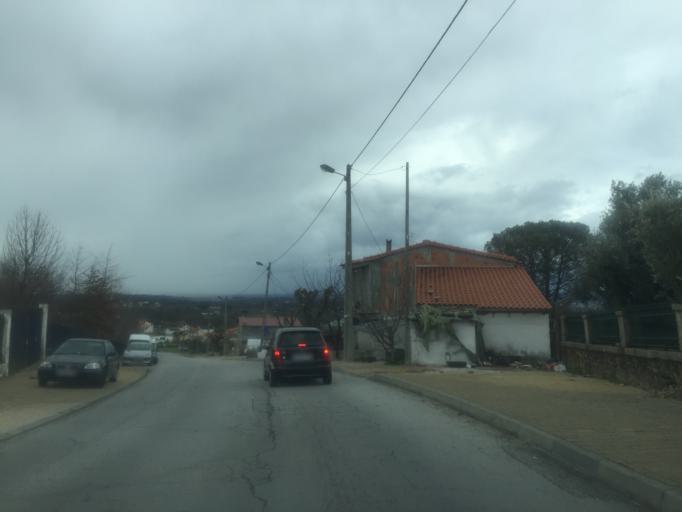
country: PT
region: Guarda
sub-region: Seia
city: Seia
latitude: 40.4044
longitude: -7.7187
